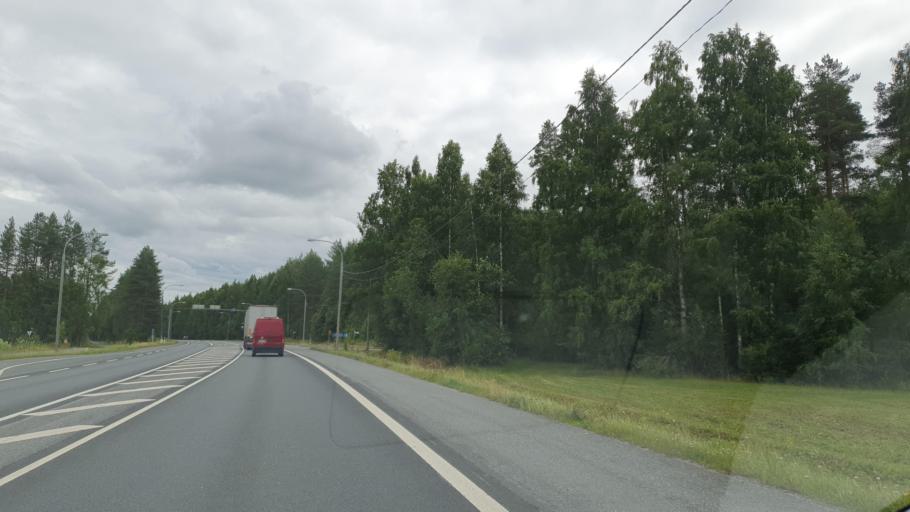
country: FI
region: Northern Savo
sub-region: Ylae-Savo
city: Iisalmi
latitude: 63.4942
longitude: 27.2715
